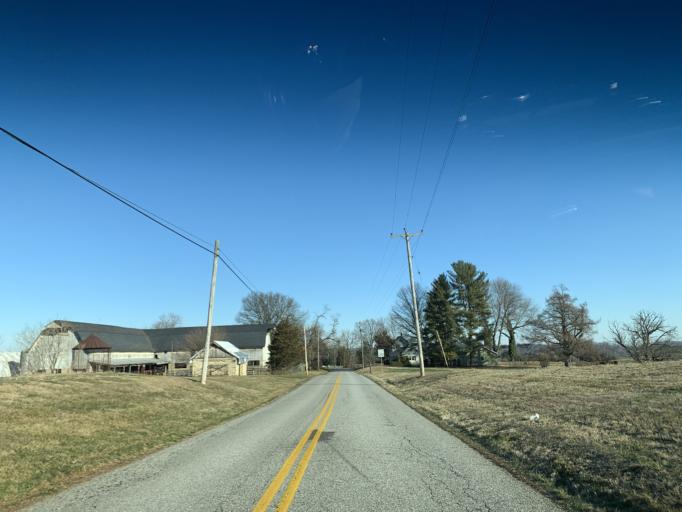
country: US
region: Maryland
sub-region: Harford County
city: Aberdeen
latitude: 39.5776
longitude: -76.2351
